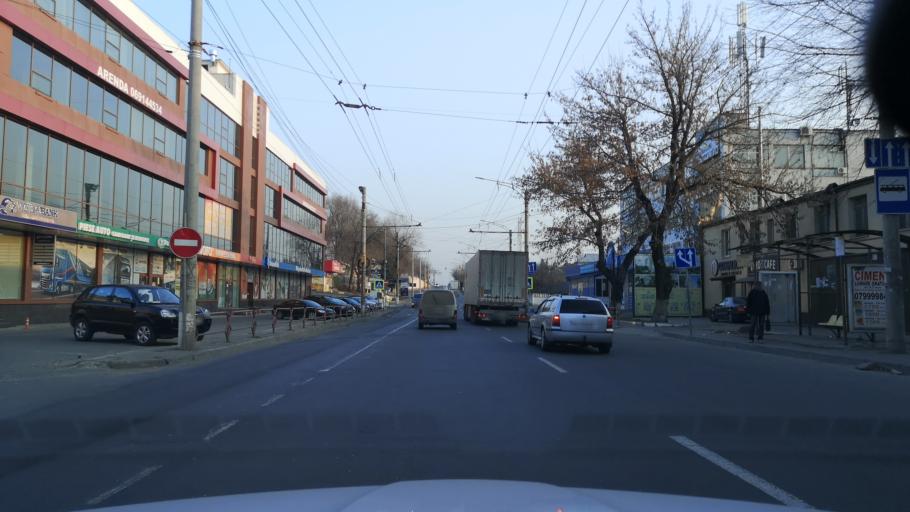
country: MD
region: Chisinau
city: Chisinau
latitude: 47.0480
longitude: 28.8263
